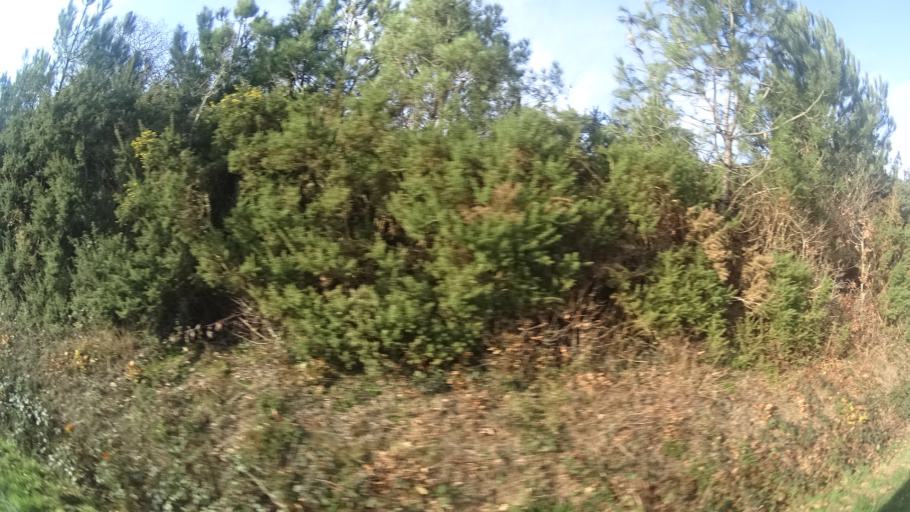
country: FR
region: Brittany
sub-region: Departement du Morbihan
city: Allaire
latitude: 47.6105
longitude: -2.1469
